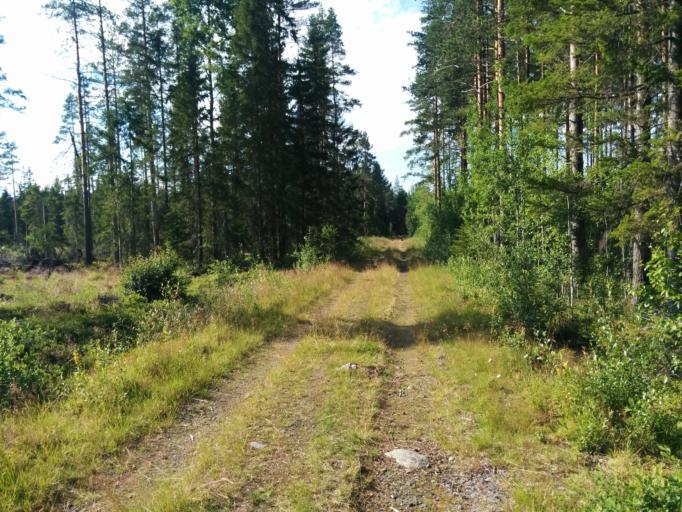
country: SE
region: Vaesterbotten
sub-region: Umea Kommun
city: Ersmark
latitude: 63.8875
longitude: 20.3035
